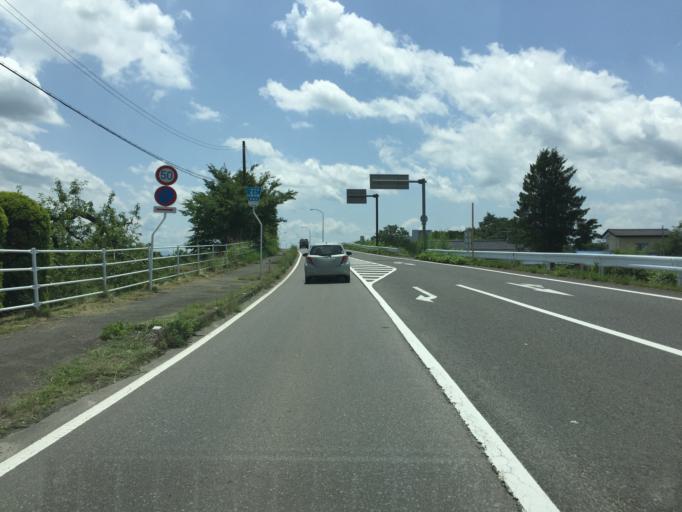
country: JP
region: Fukushima
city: Fukushima-shi
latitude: 37.7482
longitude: 140.4022
